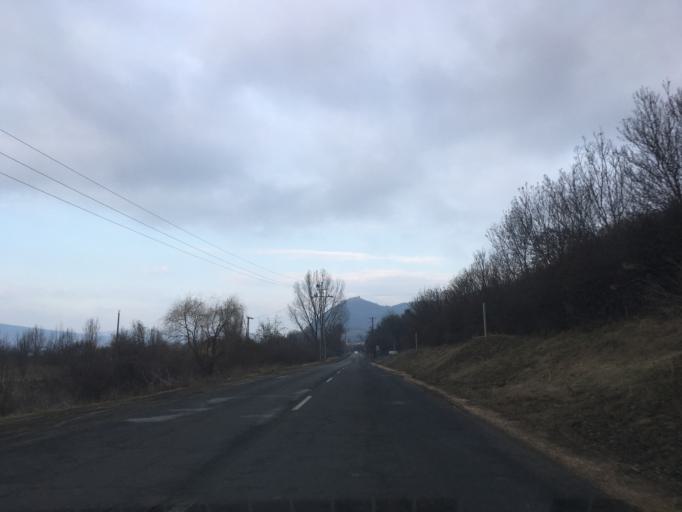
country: HU
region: Pest
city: Visegrad
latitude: 47.7723
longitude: 18.9628
